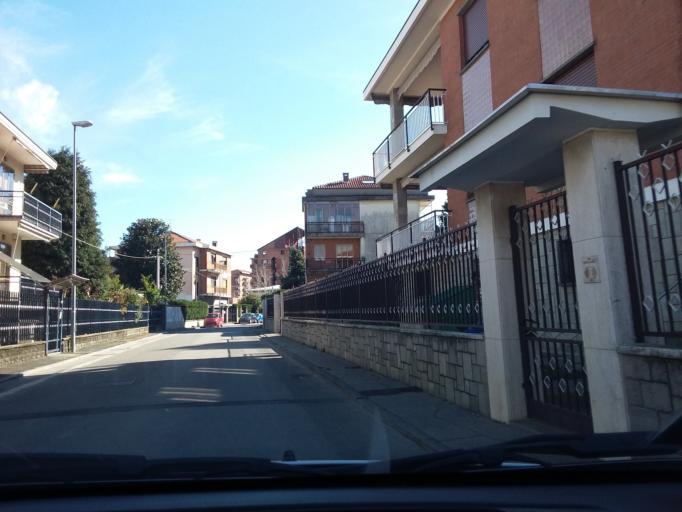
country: IT
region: Piedmont
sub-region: Provincia di Torino
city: Rivoli
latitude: 45.0783
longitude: 7.5494
